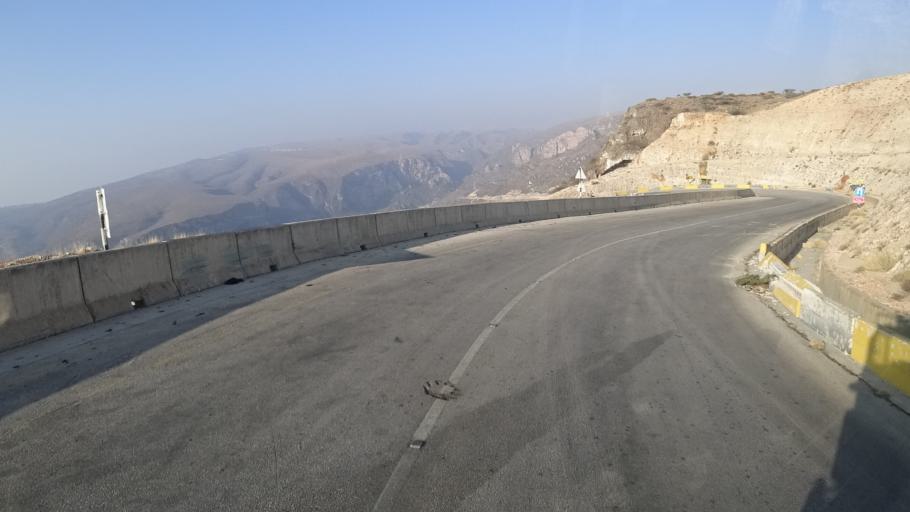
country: YE
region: Al Mahrah
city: Hawf
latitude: 16.7560
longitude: 53.2371
